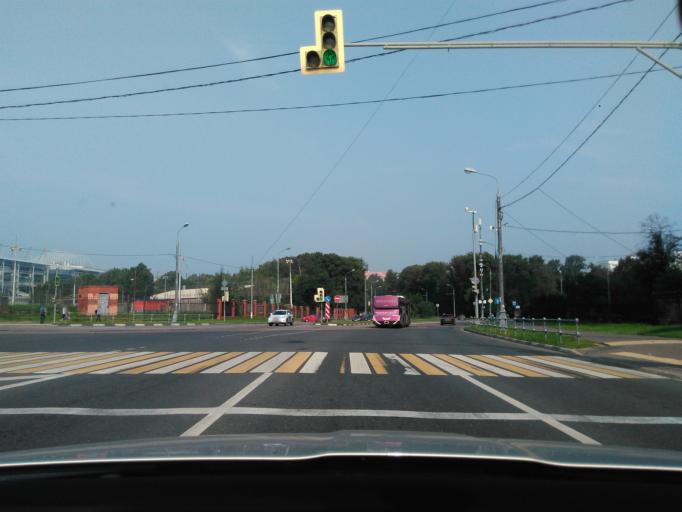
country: RU
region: Moscow
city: Sokol
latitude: 55.7925
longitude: 37.5243
